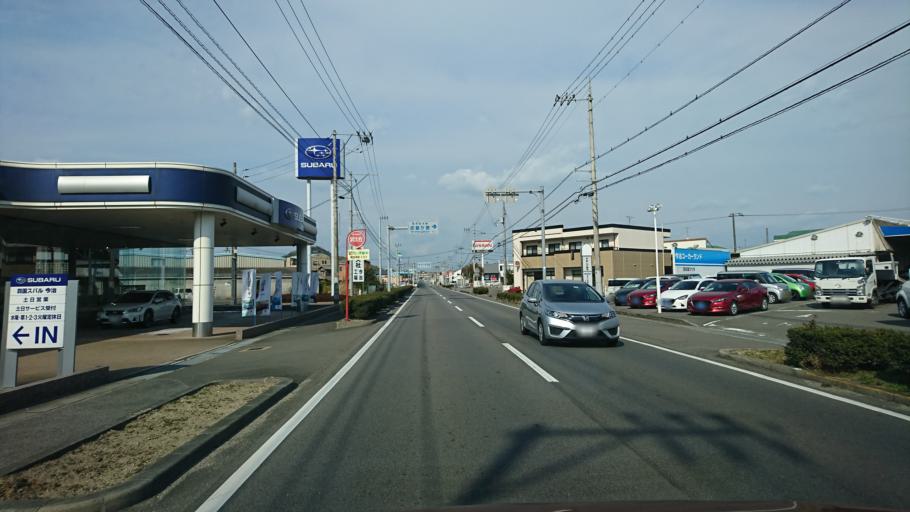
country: JP
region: Ehime
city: Saijo
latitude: 34.0140
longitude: 133.0386
